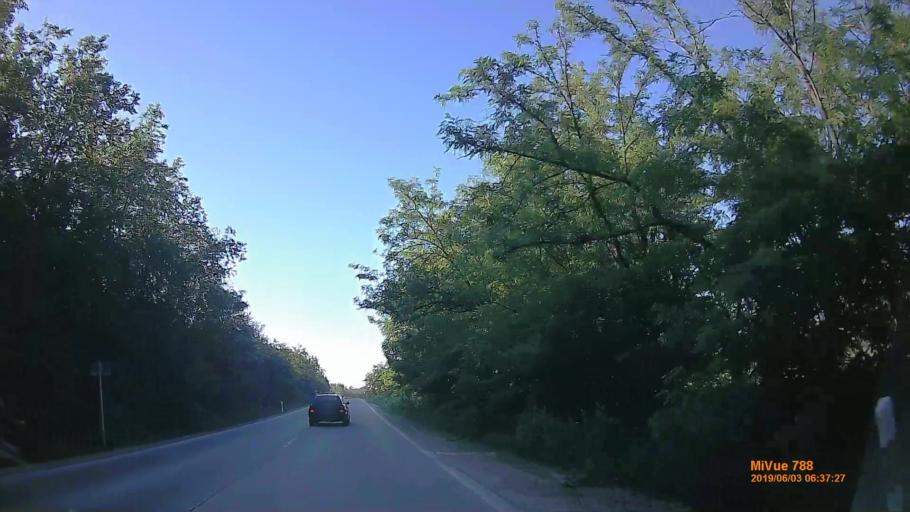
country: HU
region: Pest
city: Dunavarsany
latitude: 47.3003
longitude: 19.0883
